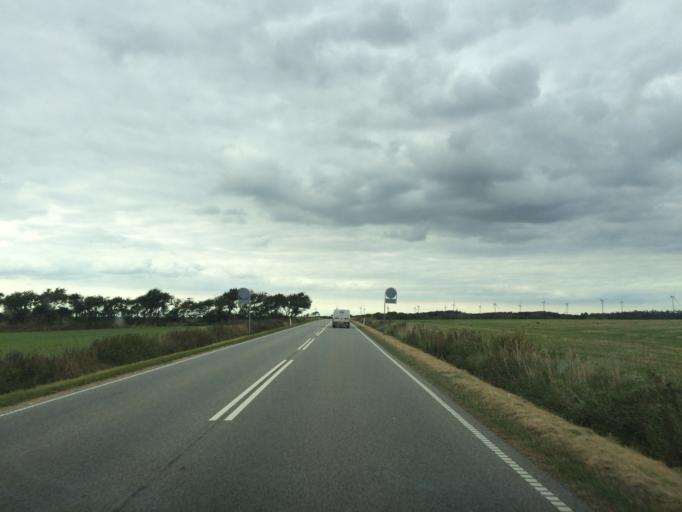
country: DK
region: Central Jutland
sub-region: Ringkobing-Skjern Kommune
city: Ringkobing
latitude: 56.0591
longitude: 8.3892
